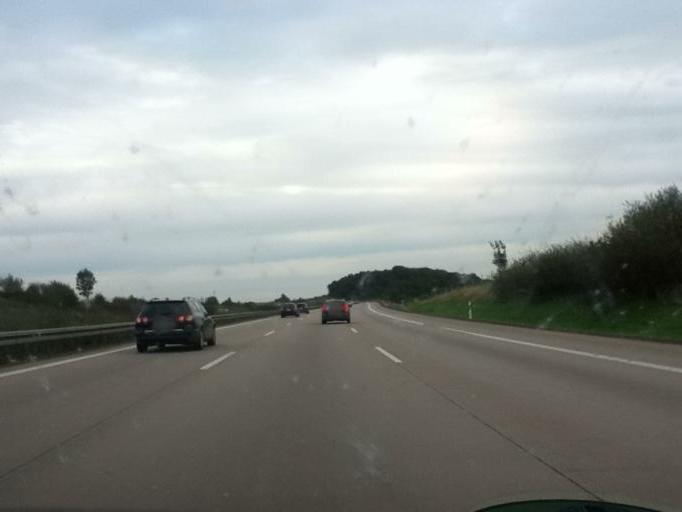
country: DE
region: Saxony
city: Reinsberg
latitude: 51.0603
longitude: 13.4216
